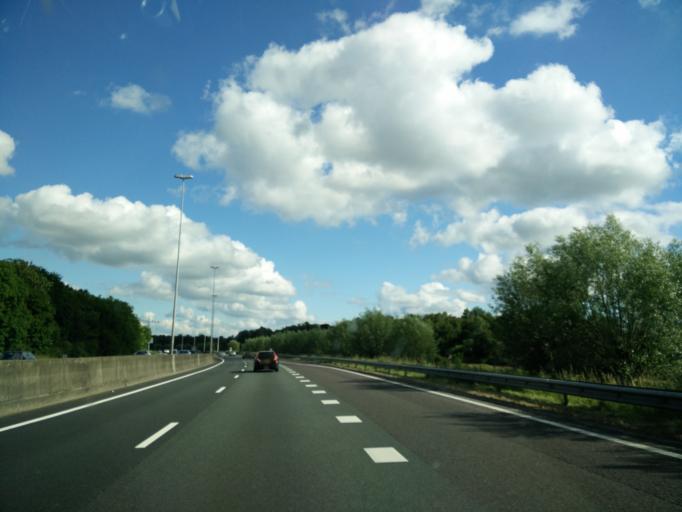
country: NL
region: Groningen
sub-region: Gemeente Groningen
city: Groningen
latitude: 53.1884
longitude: 6.5668
